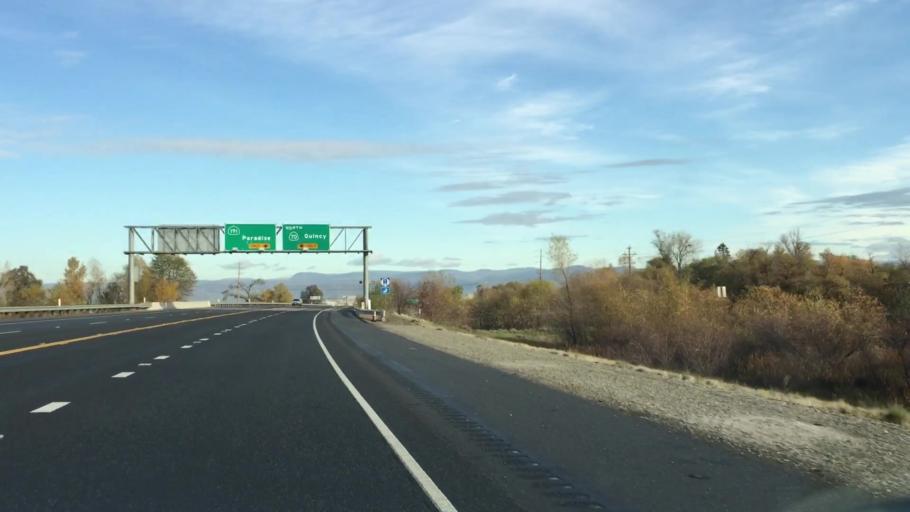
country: US
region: California
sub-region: Butte County
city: Thermalito
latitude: 39.5985
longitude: -121.6203
